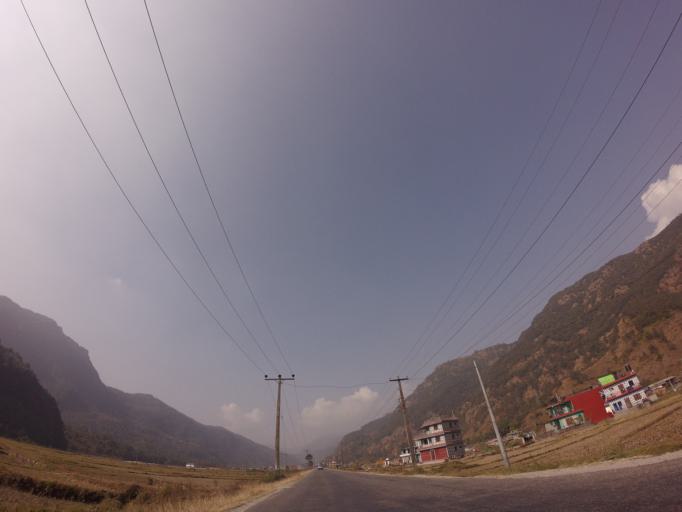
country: NP
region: Western Region
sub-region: Gandaki Zone
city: Pokhara
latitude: 28.2835
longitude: 83.9211
